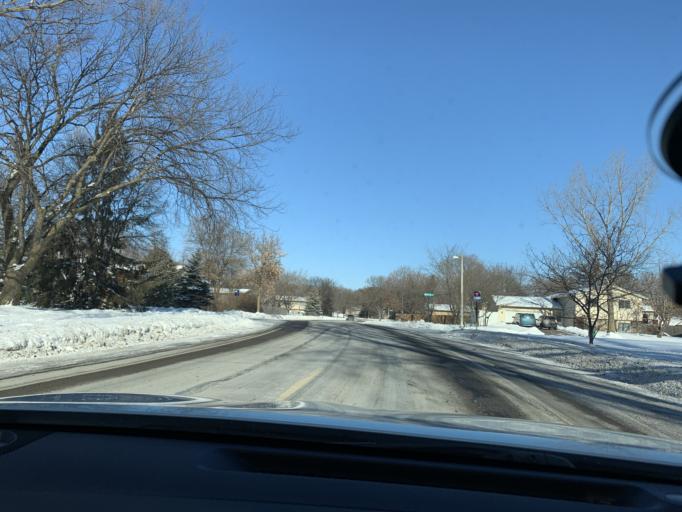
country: US
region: Minnesota
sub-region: Anoka County
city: Coon Rapids
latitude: 45.1645
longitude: -93.2995
